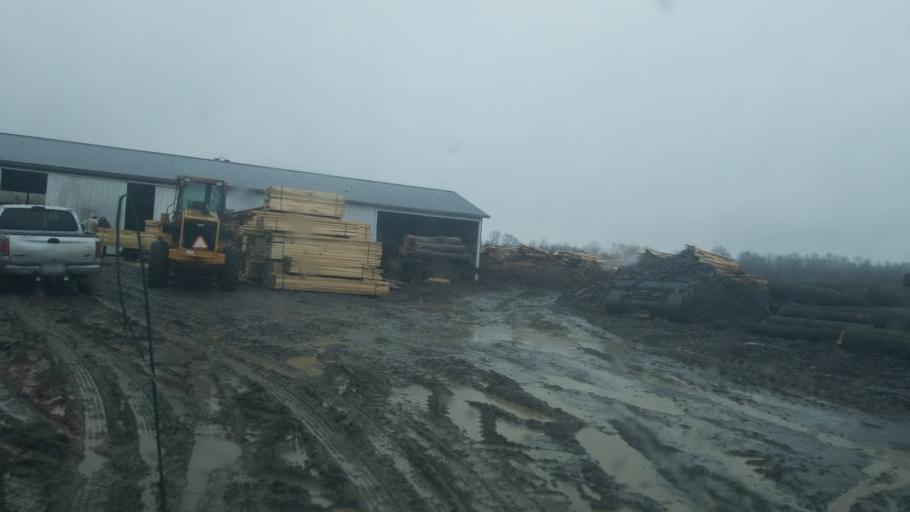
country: US
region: Ohio
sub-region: Knox County
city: Fredericktown
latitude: 40.4950
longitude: -82.6228
